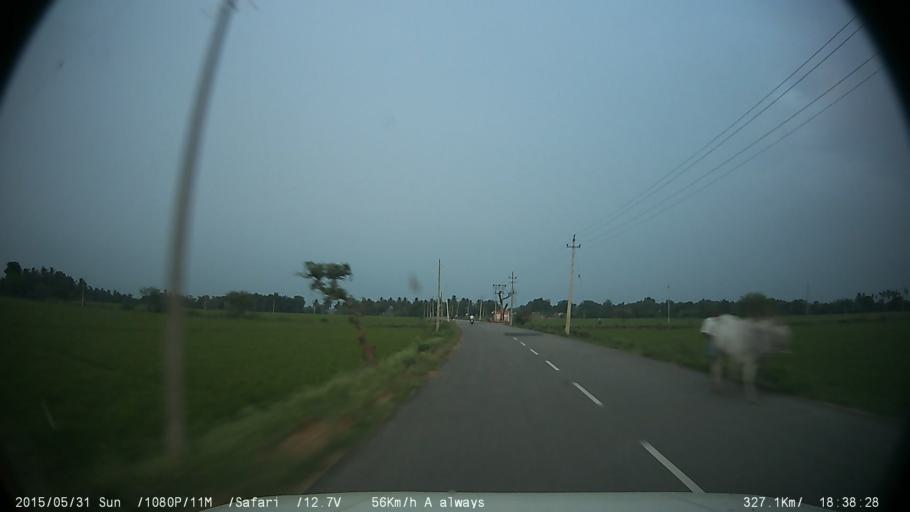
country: IN
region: Karnataka
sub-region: Mysore
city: Nanjangud
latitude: 12.1446
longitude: 76.7784
